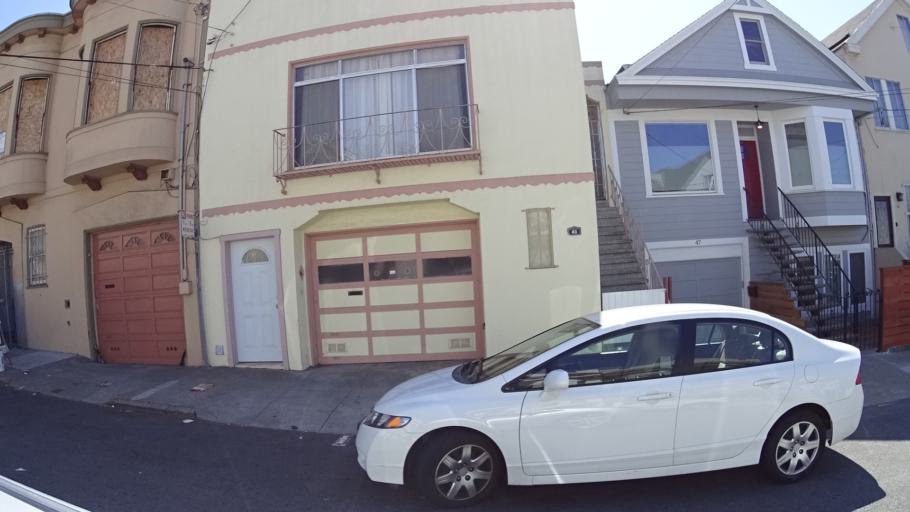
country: US
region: California
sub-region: San Mateo County
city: Daly City
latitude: 37.7256
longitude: -122.4352
